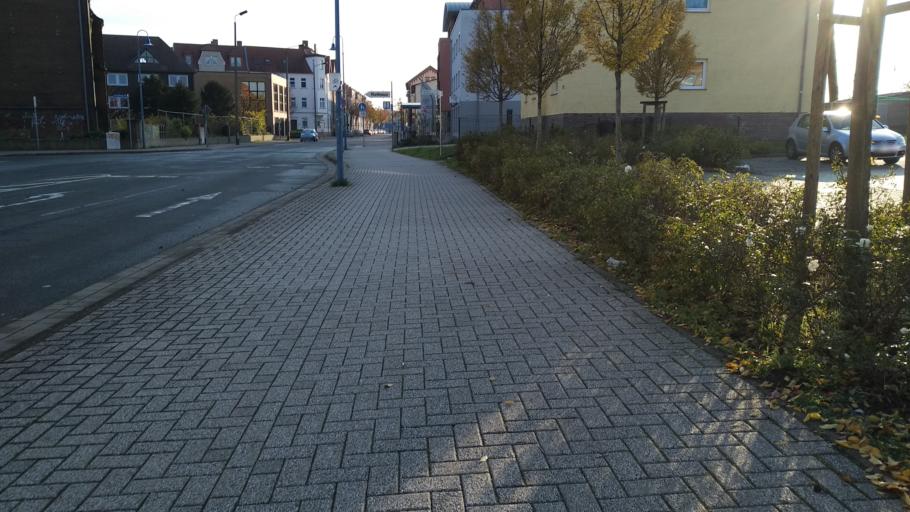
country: DE
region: Saxony
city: Bitterfeld-Wolfen
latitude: 51.6218
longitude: 12.3181
